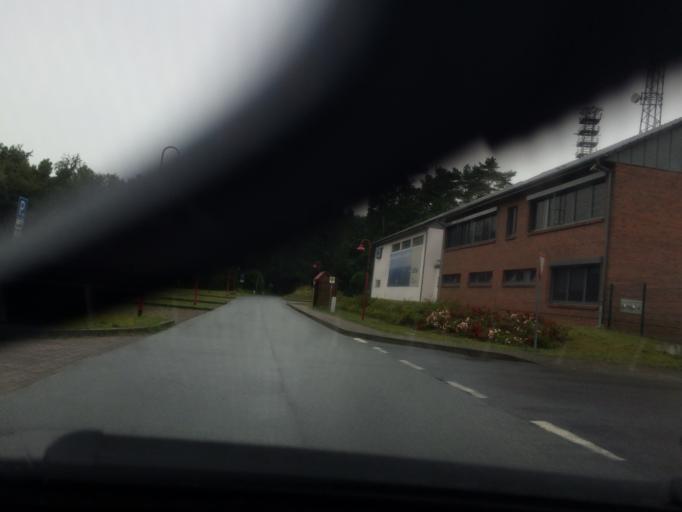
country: DE
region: Mecklenburg-Vorpommern
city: Prohn
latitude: 54.4320
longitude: 13.0280
